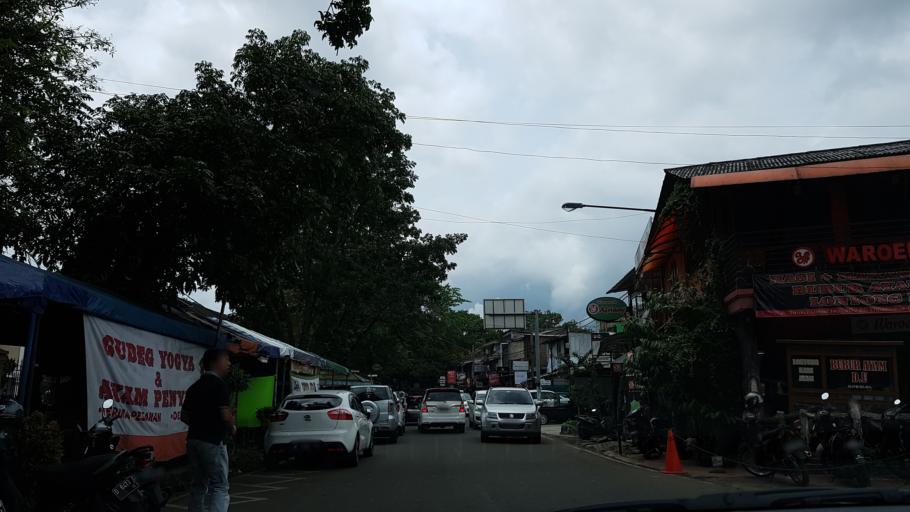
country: ID
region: West Java
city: Bandung
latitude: -6.8924
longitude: 107.6176
